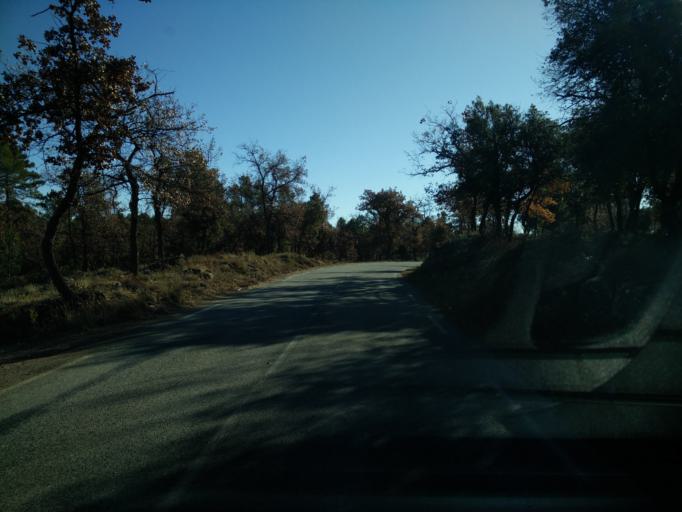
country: FR
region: Provence-Alpes-Cote d'Azur
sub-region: Departement du Var
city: Aups
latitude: 43.6014
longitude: 6.2199
